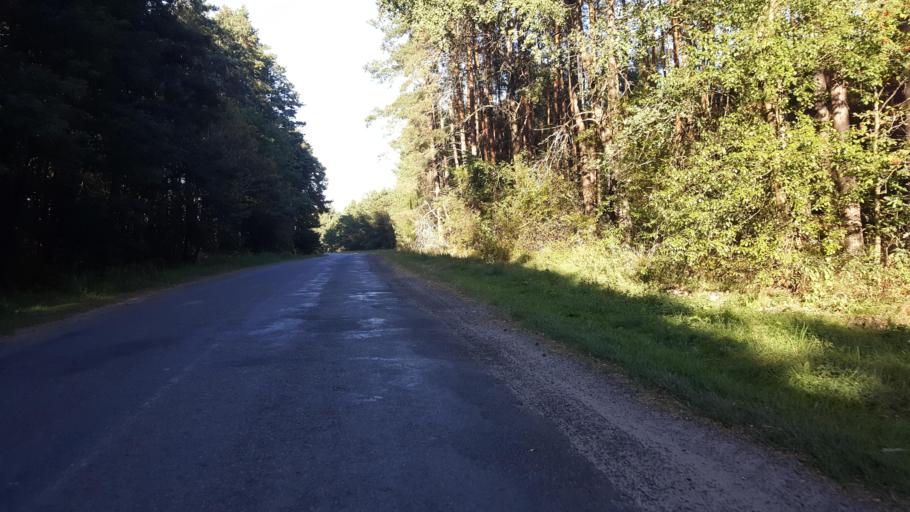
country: BY
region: Brest
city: Vysokaye
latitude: 52.3370
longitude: 23.2854
